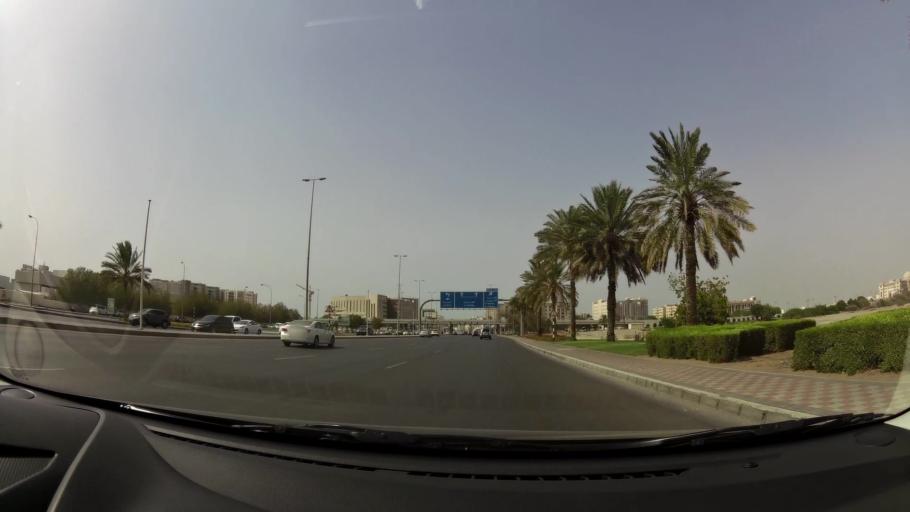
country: OM
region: Muhafazat Masqat
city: Bawshar
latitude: 23.5856
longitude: 58.3821
